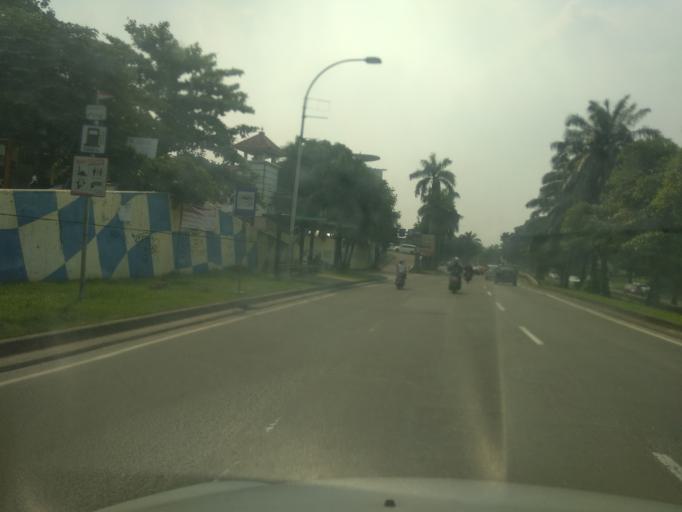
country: ID
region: West Java
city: Serpong
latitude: -6.2973
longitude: 106.6815
